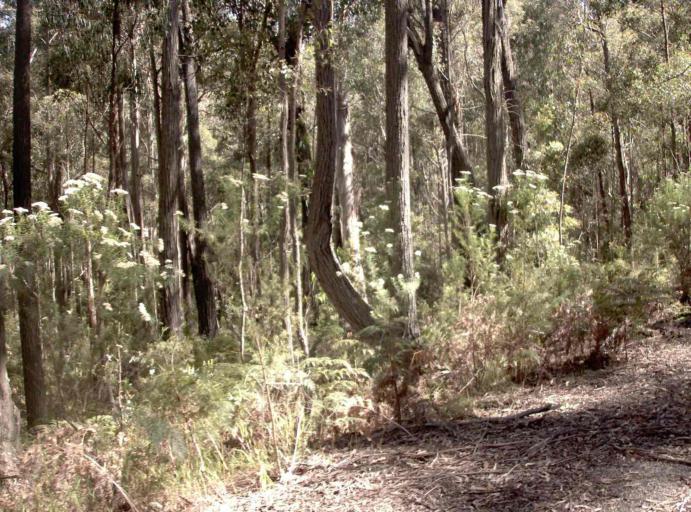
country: AU
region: New South Wales
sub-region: Bombala
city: Bombala
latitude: -37.2747
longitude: 148.7192
